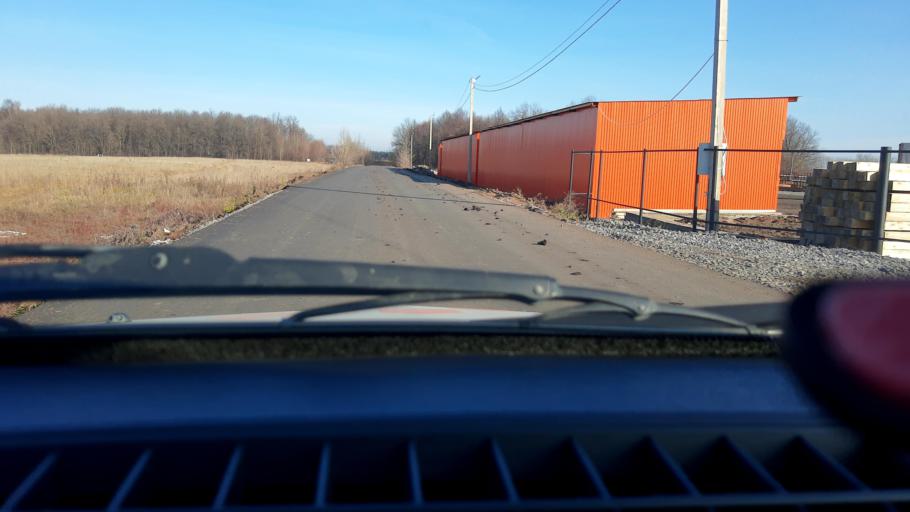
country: RU
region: Bashkortostan
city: Kabakovo
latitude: 54.6149
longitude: 56.1495
